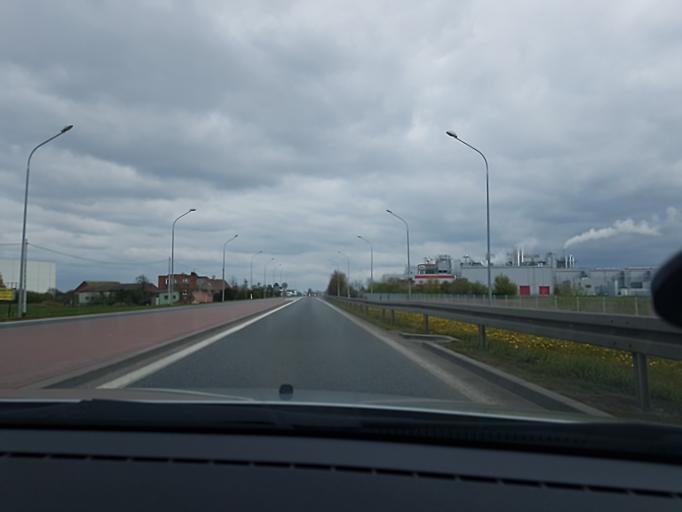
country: PL
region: Lodz Voivodeship
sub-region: Powiat kutnowski
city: Krzyzanow
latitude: 52.2227
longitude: 19.4330
